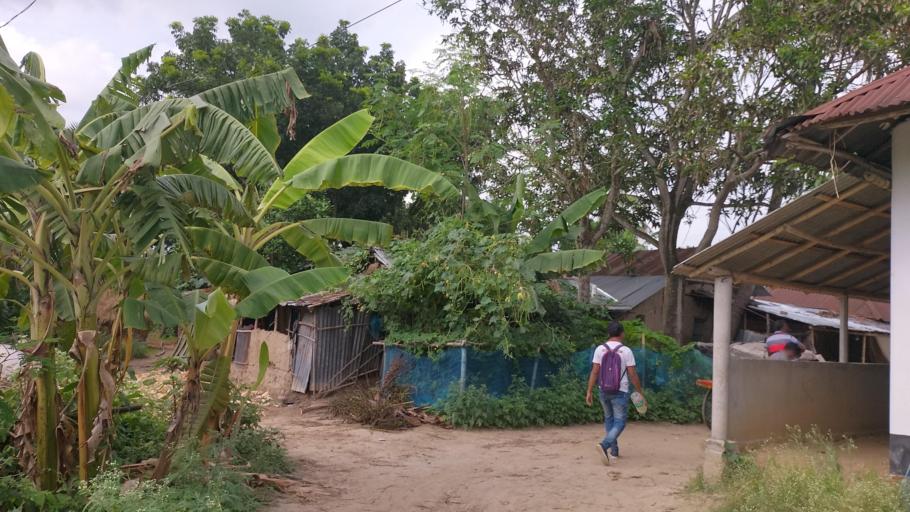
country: BD
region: Rajshahi
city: Rajshahi
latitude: 24.5551
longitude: 88.6046
